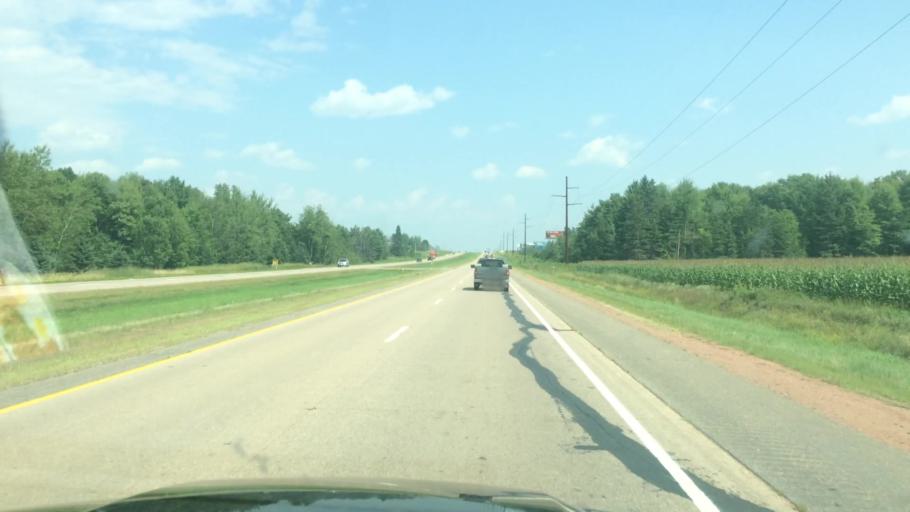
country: US
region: Wisconsin
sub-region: Marathon County
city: Edgar
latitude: 44.9441
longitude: -90.0181
